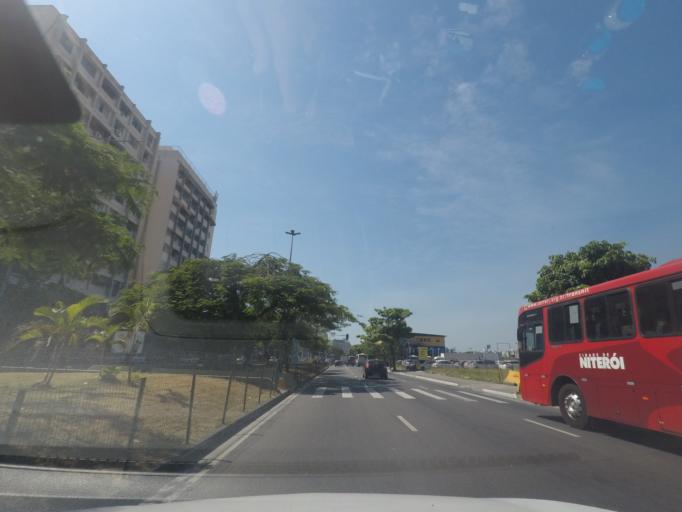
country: BR
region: Rio de Janeiro
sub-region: Niteroi
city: Niteroi
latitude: -22.8868
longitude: -43.1250
